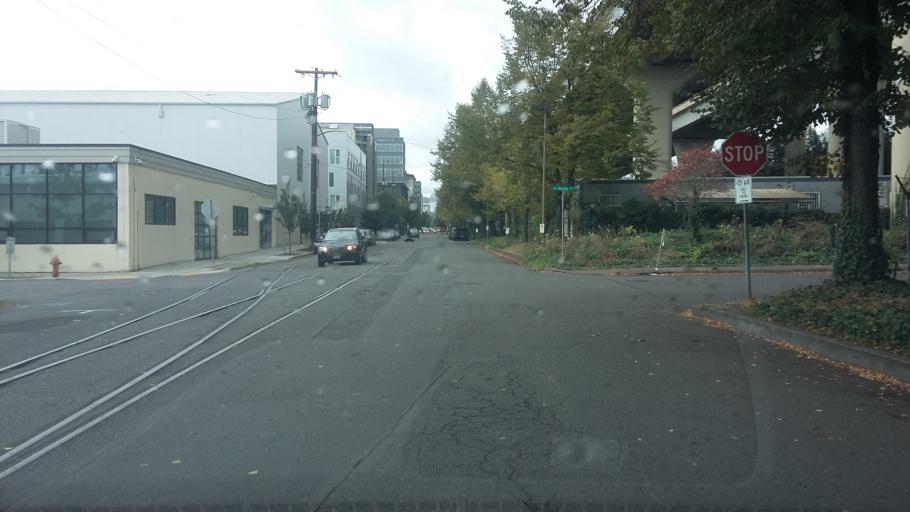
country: US
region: Oregon
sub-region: Multnomah County
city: Portland
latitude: 45.5338
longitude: -122.6866
